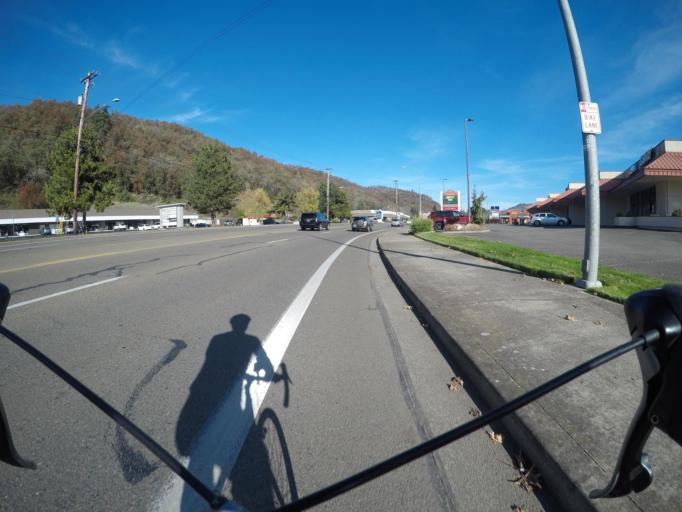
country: US
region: Oregon
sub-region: Douglas County
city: Roseburg
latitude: 43.2359
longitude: -123.3722
